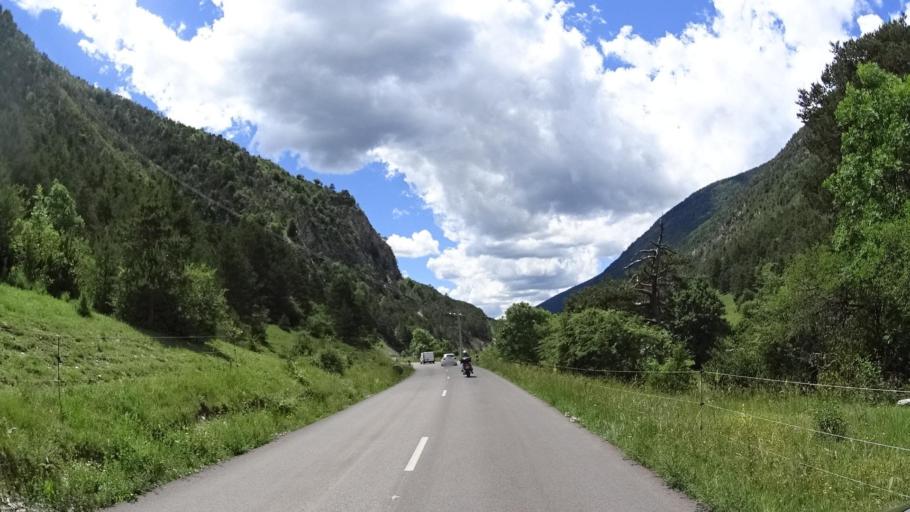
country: FR
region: Provence-Alpes-Cote d'Azur
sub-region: Departement des Alpes-de-Haute-Provence
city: Annot
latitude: 44.0558
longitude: 6.5733
